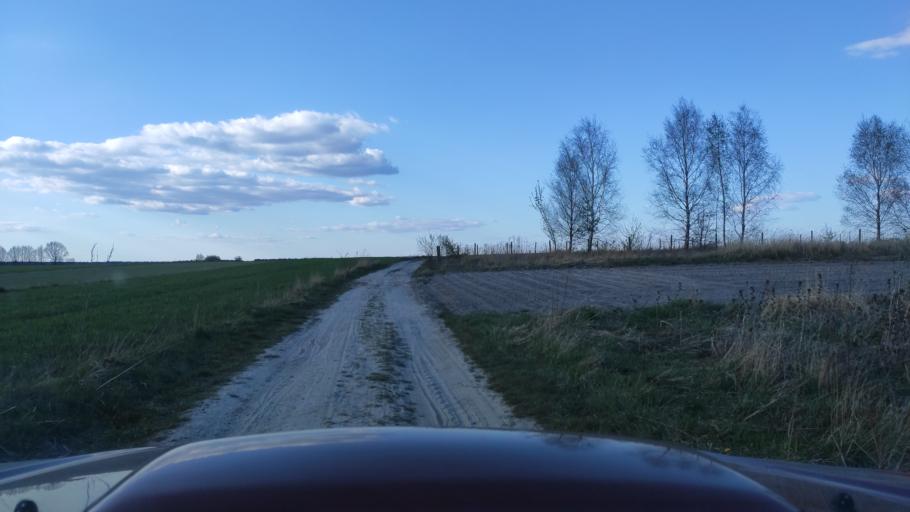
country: PL
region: Masovian Voivodeship
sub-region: Powiat zwolenski
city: Zwolen
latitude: 51.3721
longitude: 21.5753
